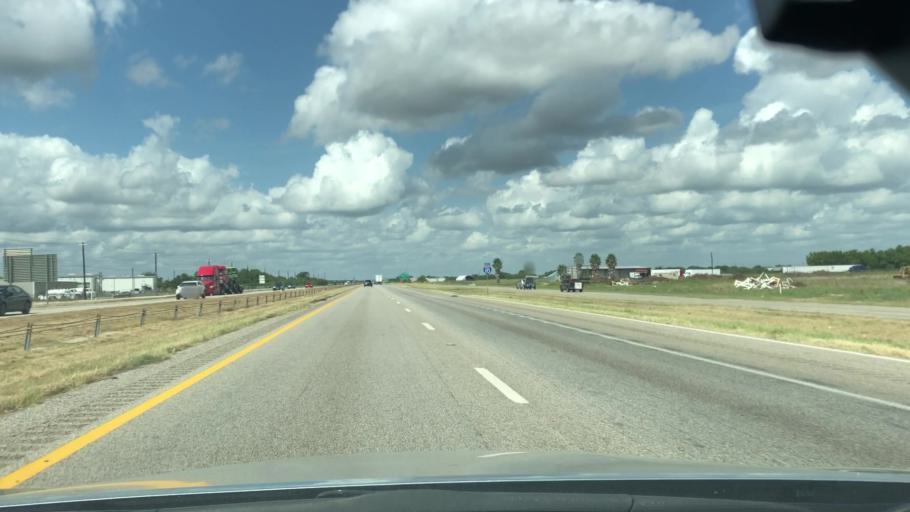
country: US
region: Texas
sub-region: Guadalupe County
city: Marion
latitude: 29.5128
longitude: -98.1555
